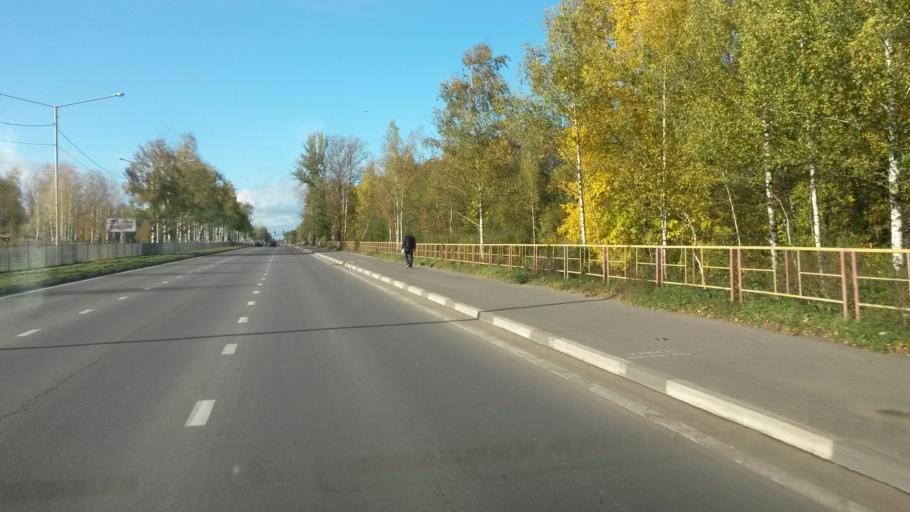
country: RU
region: Jaroslavl
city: Yaroslavl
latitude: 57.5581
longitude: 39.9388
